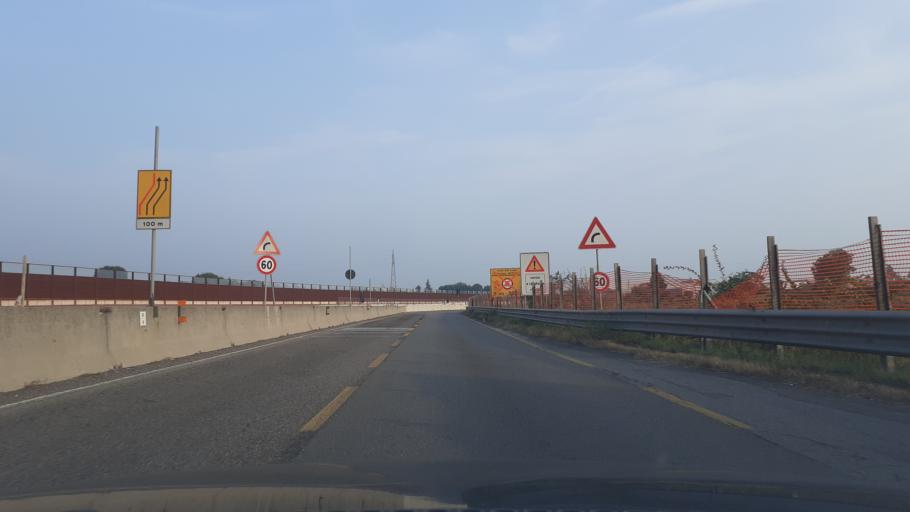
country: IT
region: Lombardy
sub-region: Citta metropolitana di Milano
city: Cormano
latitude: 45.5535
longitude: 9.1458
